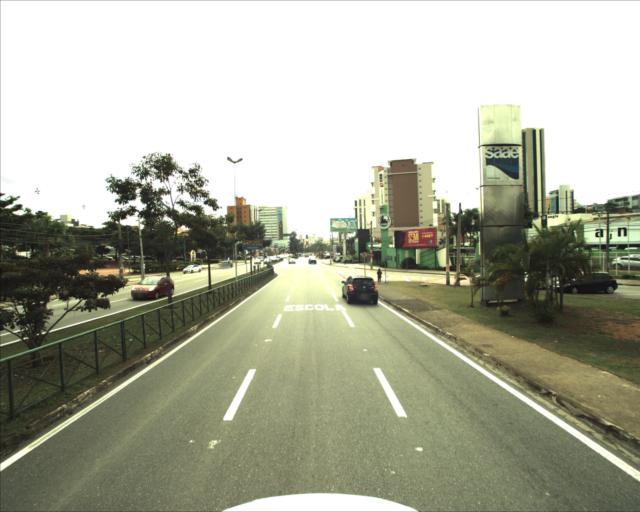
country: BR
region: Sao Paulo
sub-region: Sorocaba
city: Sorocaba
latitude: -23.5233
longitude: -47.4648
